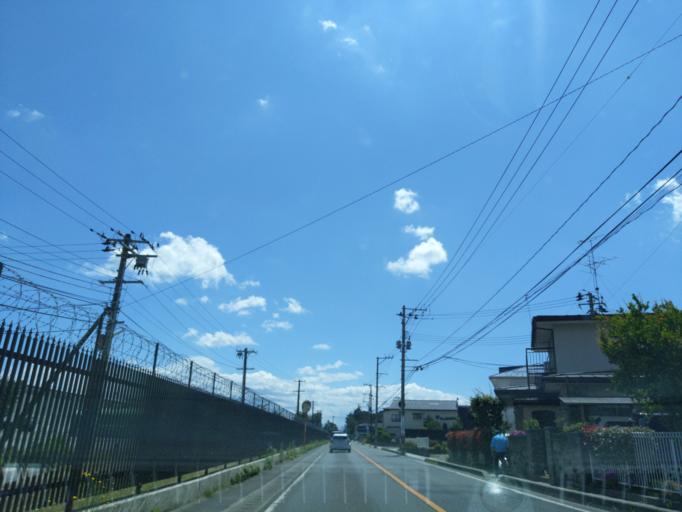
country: JP
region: Fukushima
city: Koriyama
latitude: 37.3987
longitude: 140.3238
